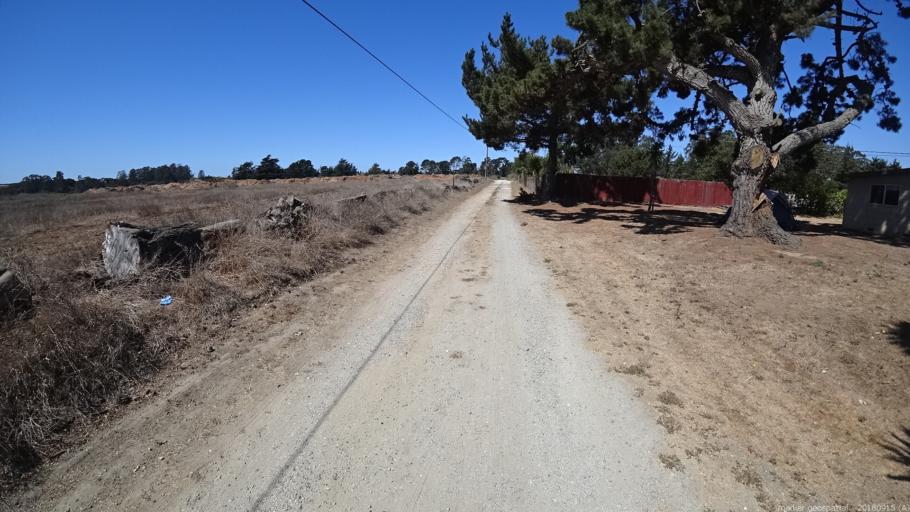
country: US
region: California
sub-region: Monterey County
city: Las Lomas
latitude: 36.8673
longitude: -121.7529
